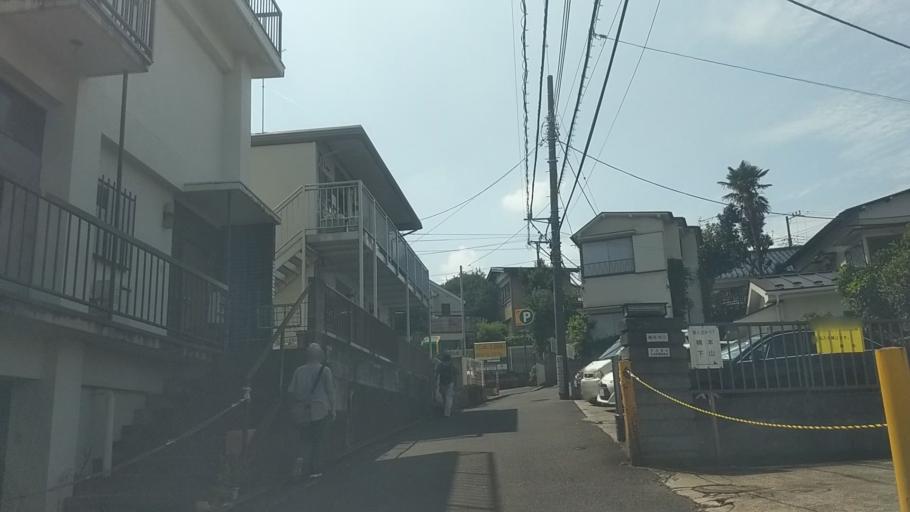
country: JP
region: Kanagawa
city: Yokohama
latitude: 35.4788
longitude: 139.6258
